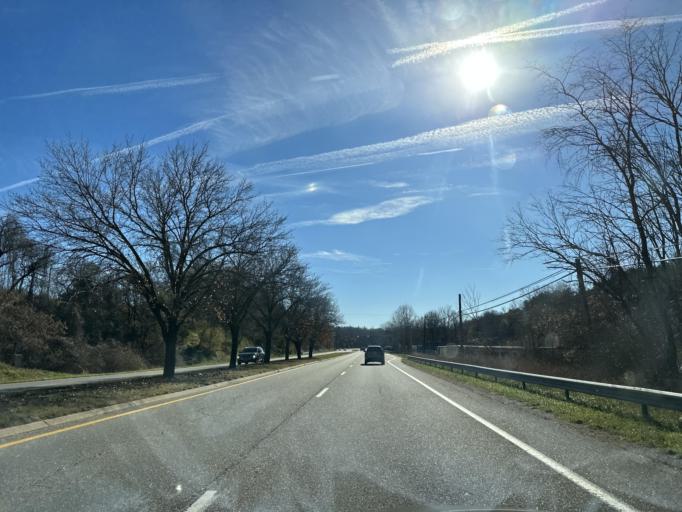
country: US
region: Virginia
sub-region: Augusta County
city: Fishersville
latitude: 38.1177
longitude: -79.0192
